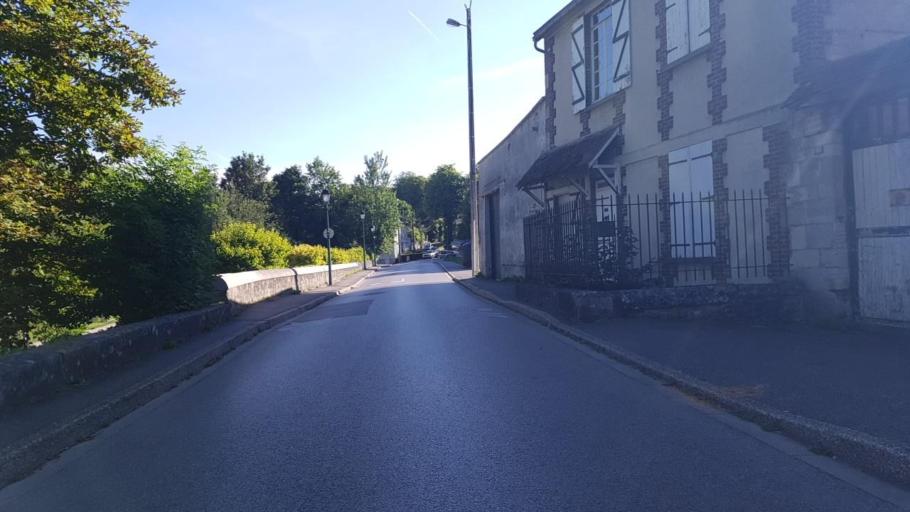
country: FR
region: Picardie
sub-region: Departement de l'Oise
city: Senlis
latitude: 49.2133
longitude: 2.5919
